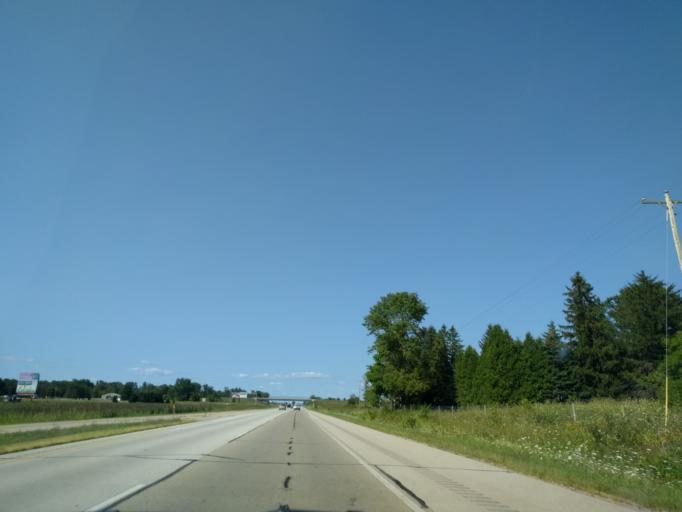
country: US
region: Wisconsin
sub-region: Brown County
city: Suamico
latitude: 44.7447
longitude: -88.0506
